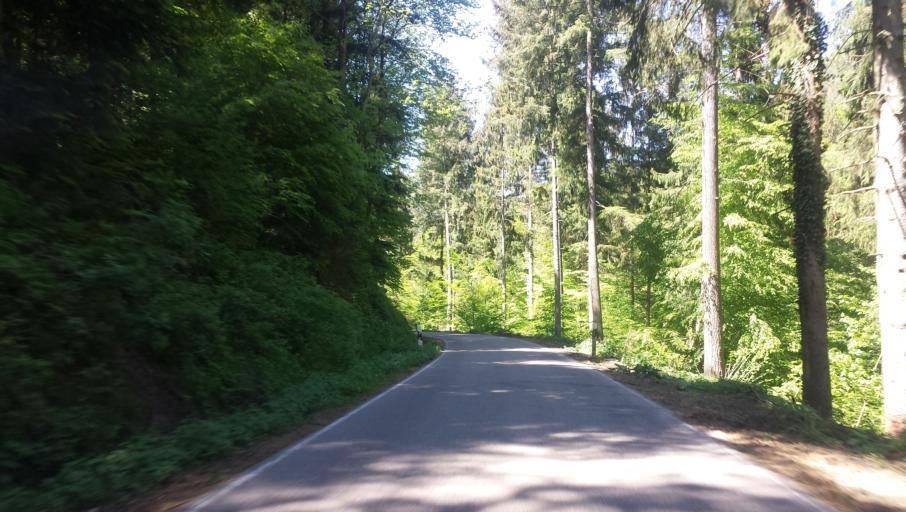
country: DE
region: Rheinland-Pfalz
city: Ramberg
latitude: 49.2813
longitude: 8.0233
